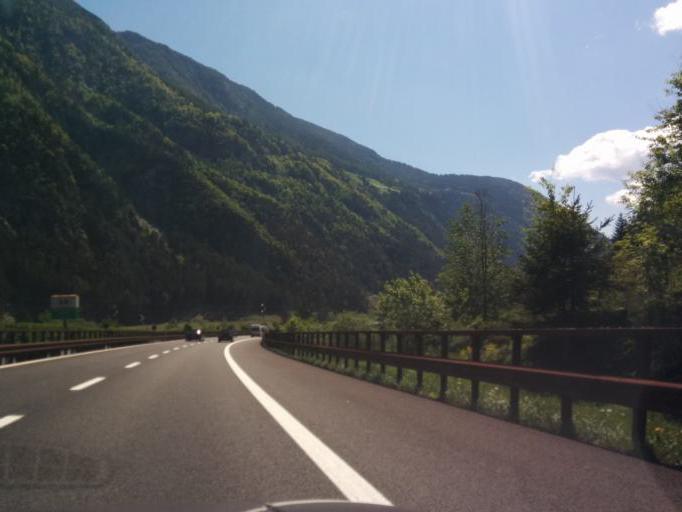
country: IT
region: Trentino-Alto Adige
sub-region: Bolzano
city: Campo di Trens
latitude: 46.8459
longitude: 11.5200
